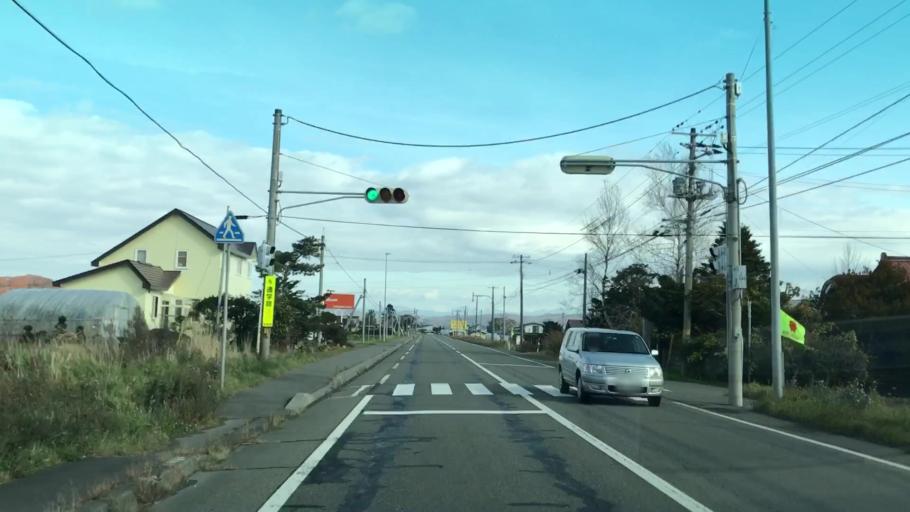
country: JP
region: Hokkaido
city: Shizunai-furukawacho
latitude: 42.5482
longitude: 142.0666
